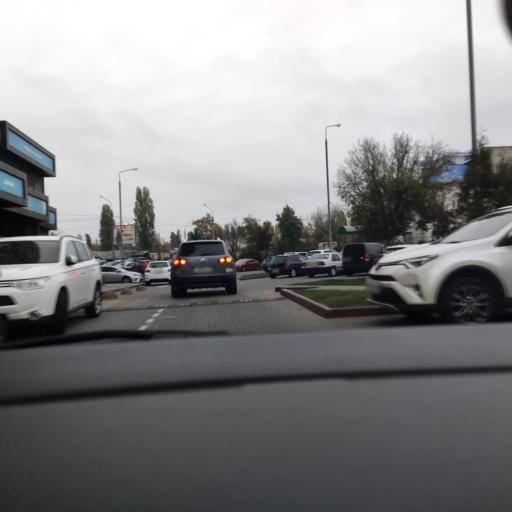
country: RU
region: Voronezj
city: Voronezh
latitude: 51.6549
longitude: 39.1803
